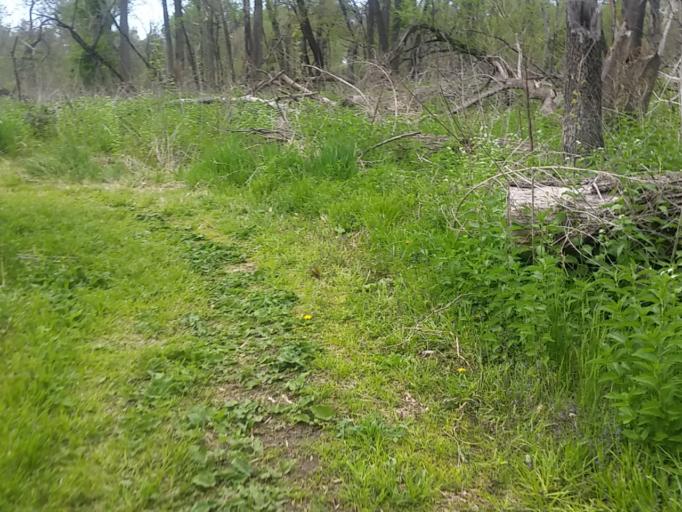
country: US
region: Nebraska
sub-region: Sarpy County
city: Bellevue
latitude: 41.1795
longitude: -95.8969
